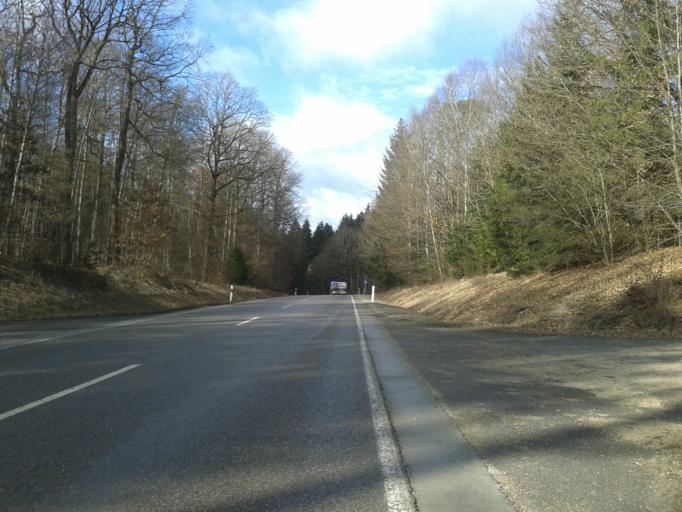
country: DE
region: Baden-Wuerttemberg
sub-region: Tuebingen Region
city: Altheim
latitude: 48.3482
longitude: 9.7954
